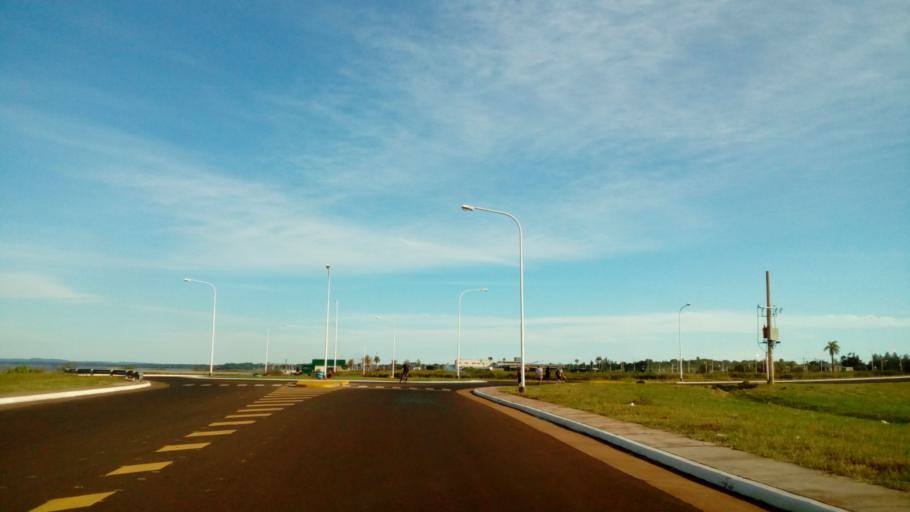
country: AR
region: Misiones
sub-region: Departamento de Capital
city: Posadas
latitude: -27.4227
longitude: -55.8736
